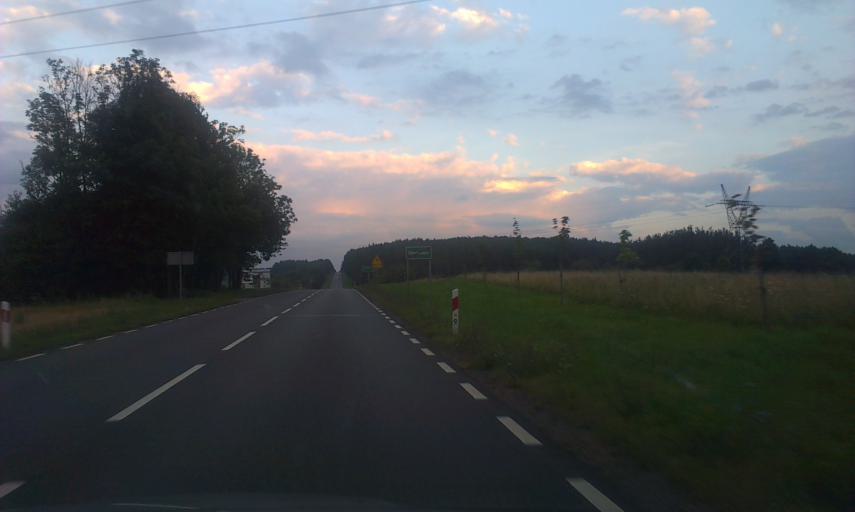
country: PL
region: West Pomeranian Voivodeship
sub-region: Powiat koszalinski
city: Sianow
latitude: 54.1216
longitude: 16.3088
